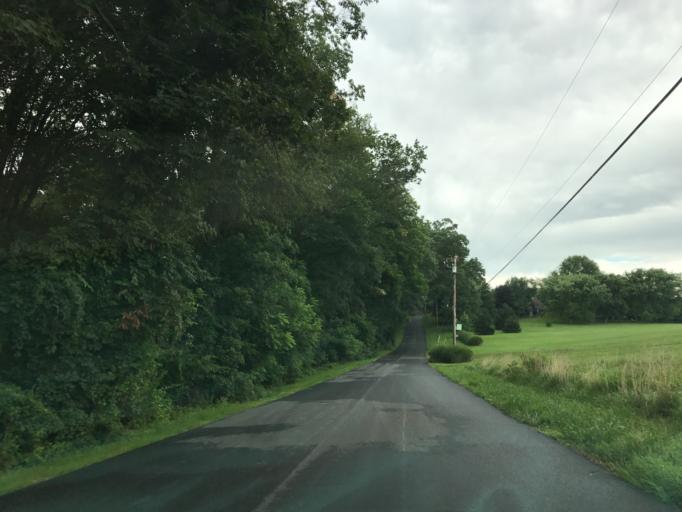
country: US
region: Pennsylvania
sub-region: York County
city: New Freedom
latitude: 39.6753
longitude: -76.7382
